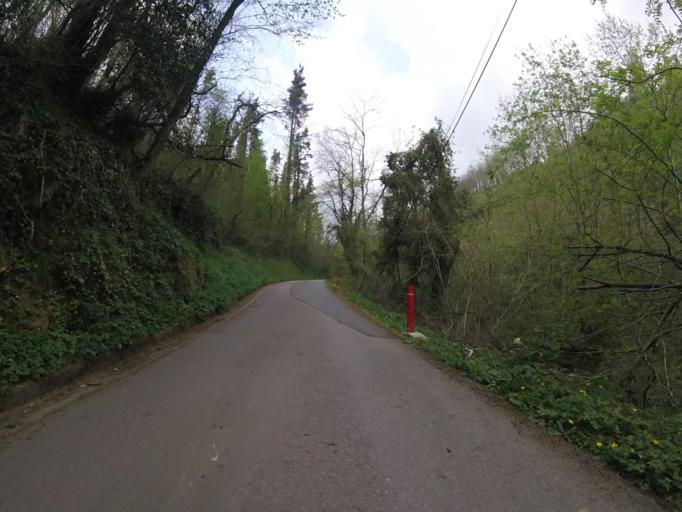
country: ES
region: Basque Country
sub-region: Provincia de Guipuzcoa
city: Anoeta
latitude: 43.1677
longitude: -2.0790
